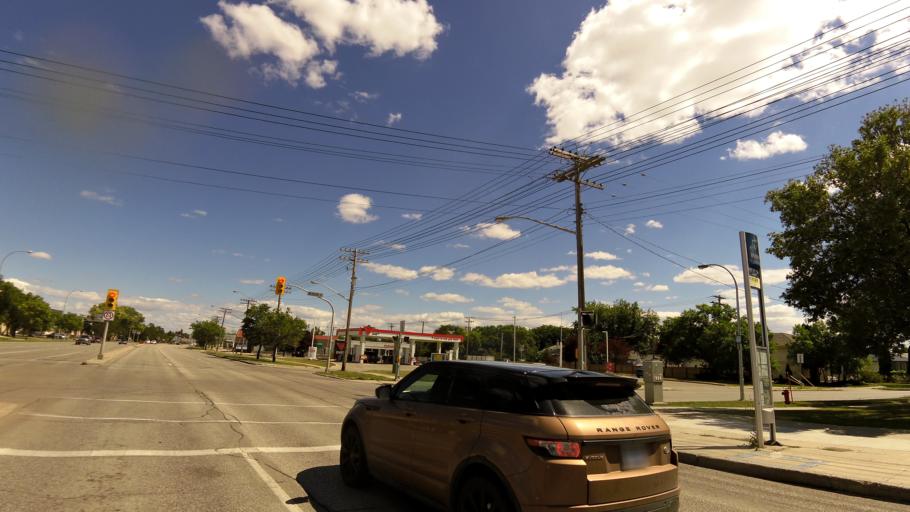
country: CA
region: Manitoba
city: Headingley
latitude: 49.8827
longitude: -97.3075
